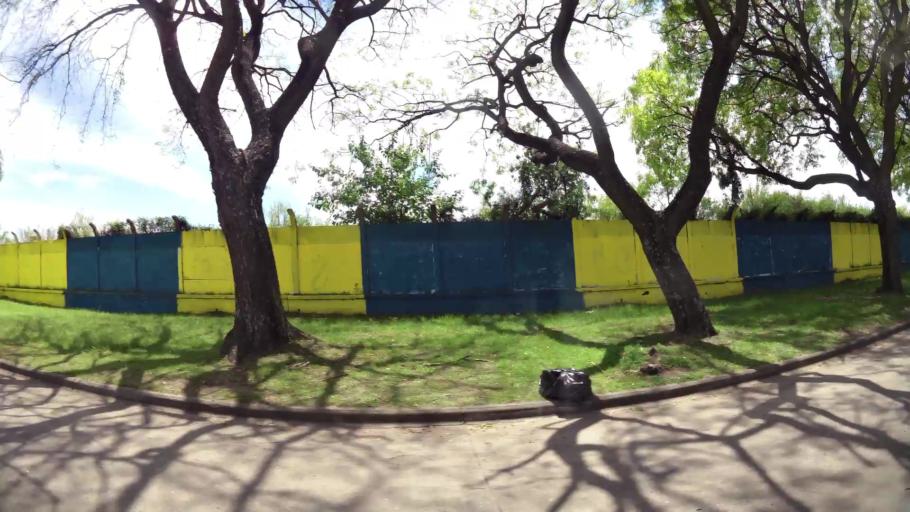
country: AR
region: Santa Fe
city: Gobernador Galvez
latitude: -32.9900
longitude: -60.6267
